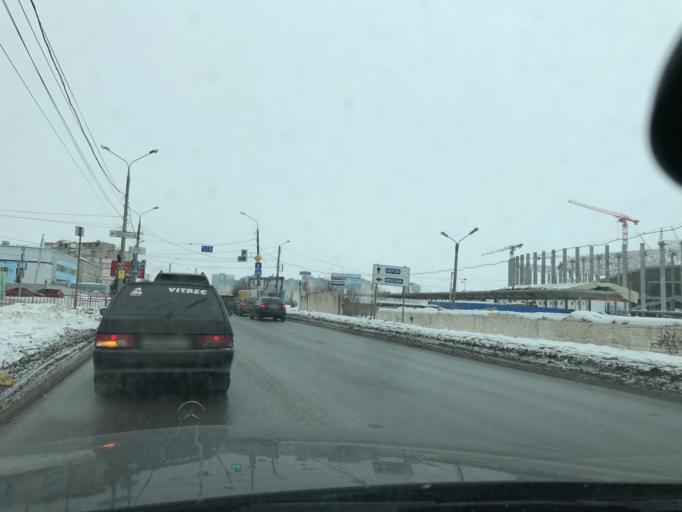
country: RU
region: Nizjnij Novgorod
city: Nizhniy Novgorod
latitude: 56.3329
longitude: 43.9641
